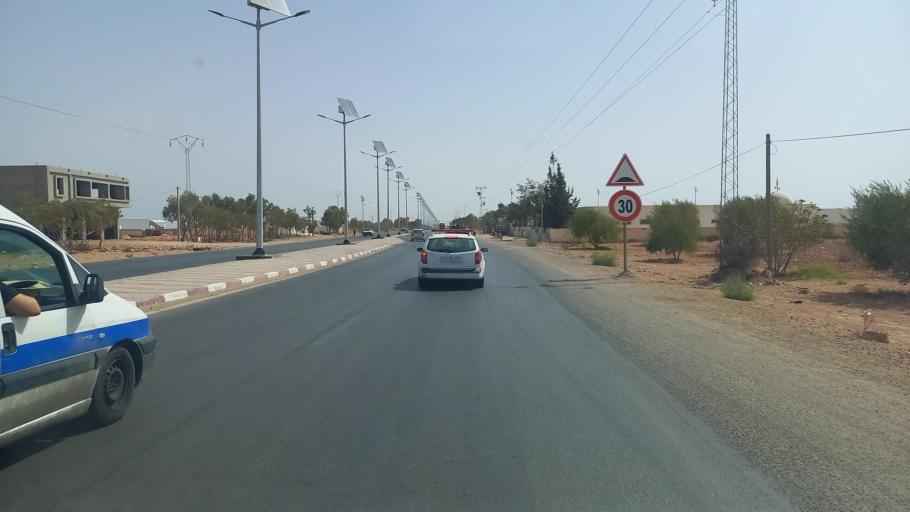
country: TN
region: Madanin
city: Medenine
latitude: 33.3555
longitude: 10.5429
